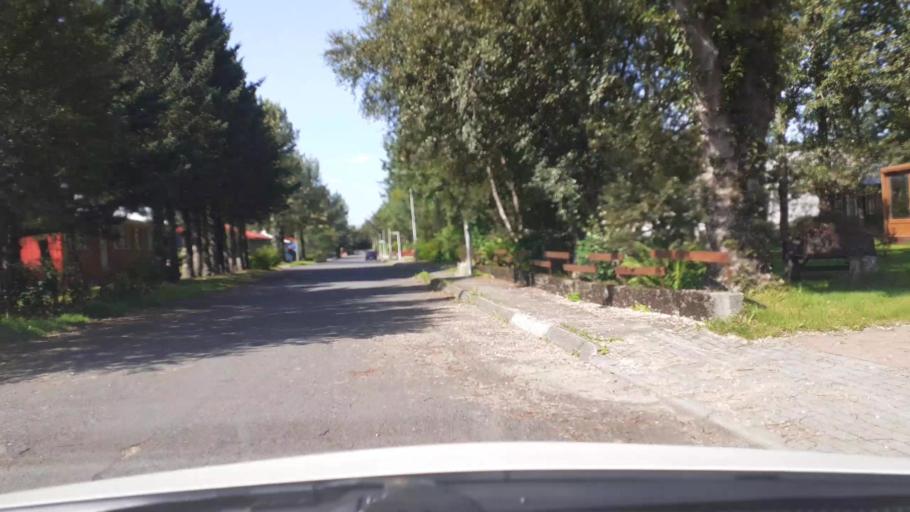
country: IS
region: South
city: Selfoss
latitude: 63.9286
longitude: -21.0074
